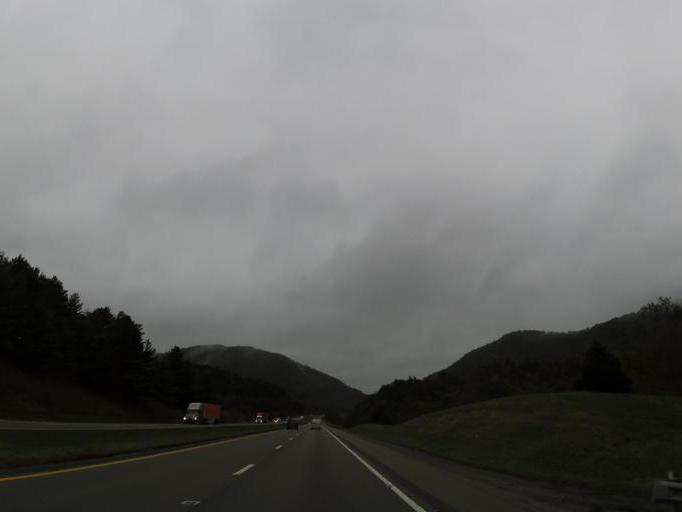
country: US
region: Virginia
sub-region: Wythe County
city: Wytheville
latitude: 37.0028
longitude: -81.0942
